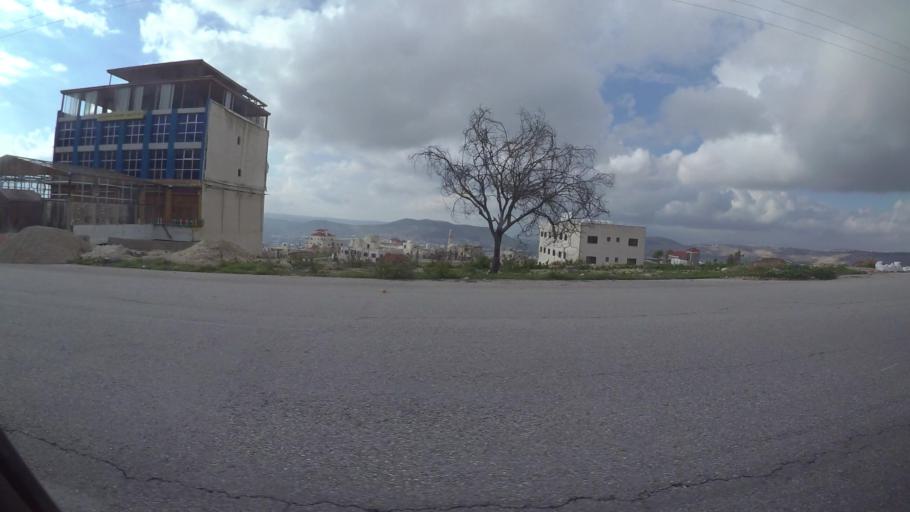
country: JO
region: Amman
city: Al Jubayhah
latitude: 32.0689
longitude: 35.8735
